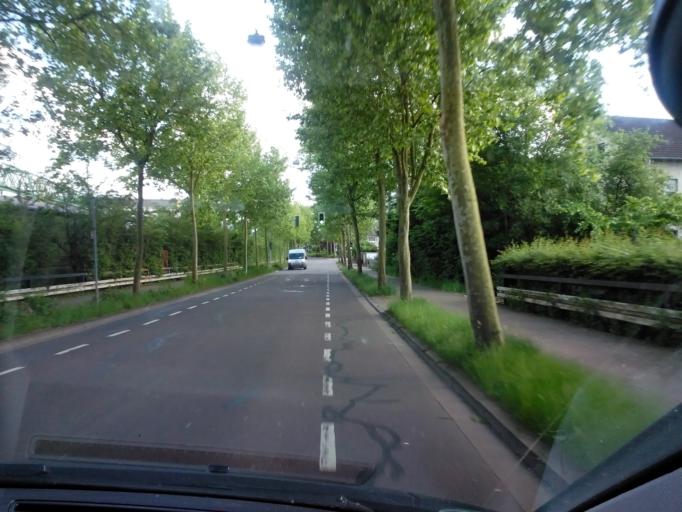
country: DE
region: Saarland
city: Dillingen
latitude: 49.3553
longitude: 6.7159
